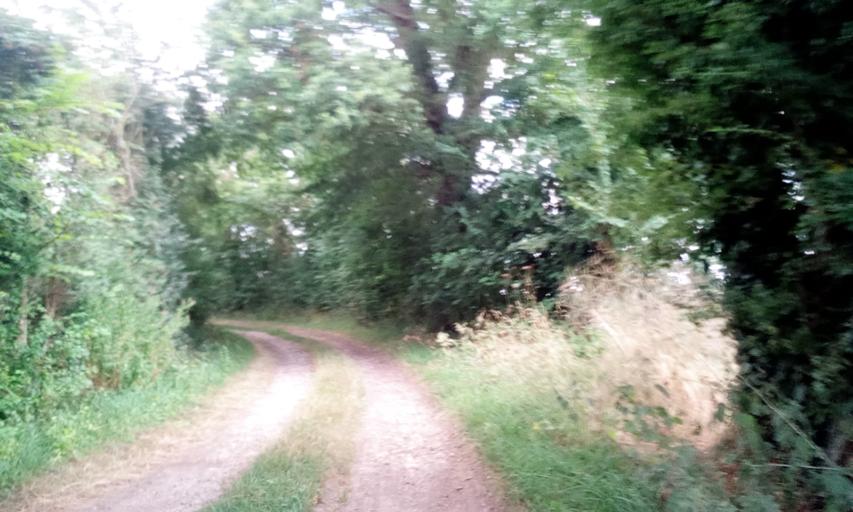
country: FR
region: Lower Normandy
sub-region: Departement du Calvados
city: Troarn
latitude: 49.1640
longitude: -0.1888
